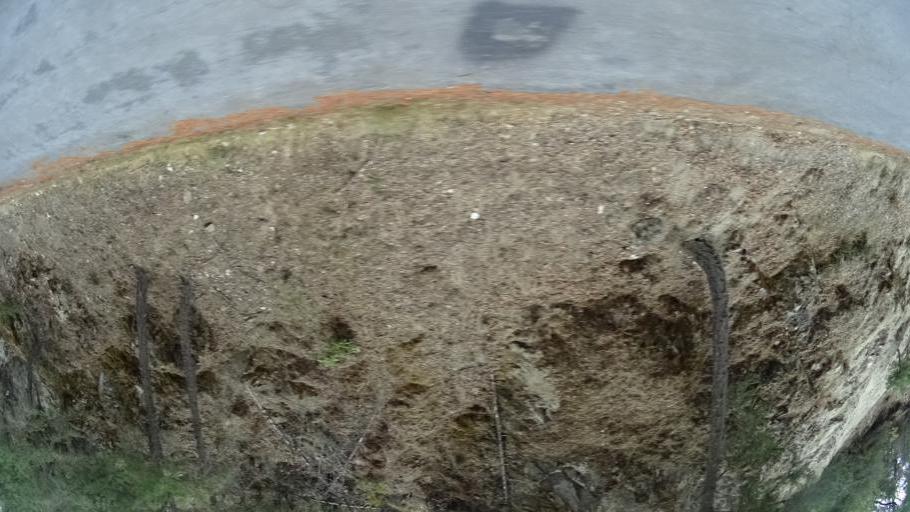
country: US
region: California
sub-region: Siskiyou County
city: Happy Camp
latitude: 41.8363
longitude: -123.1987
